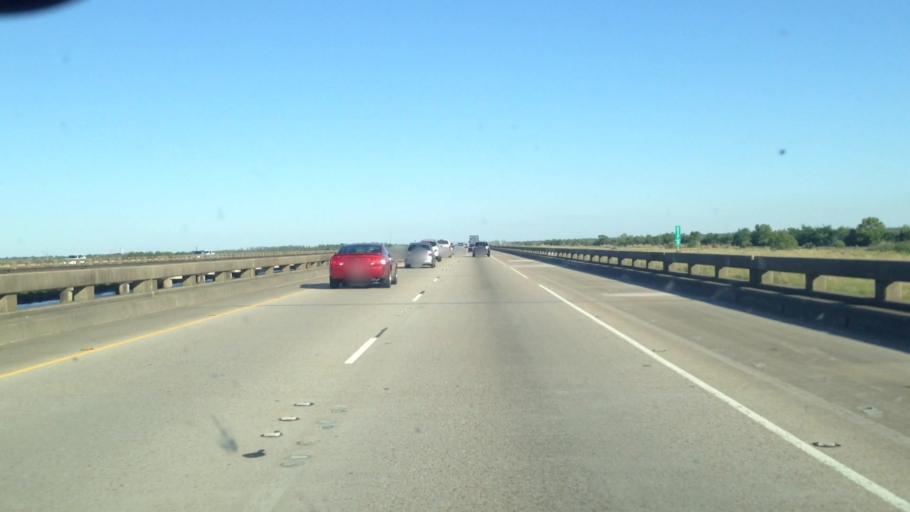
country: US
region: Louisiana
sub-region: Saint Charles Parish
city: Saint Rose
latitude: 30.0238
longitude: -90.3253
